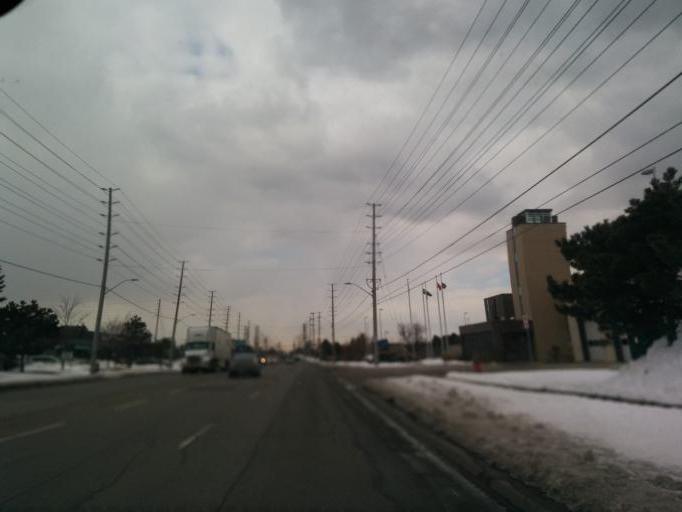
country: CA
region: Ontario
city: Mississauga
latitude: 43.6615
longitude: -79.6792
